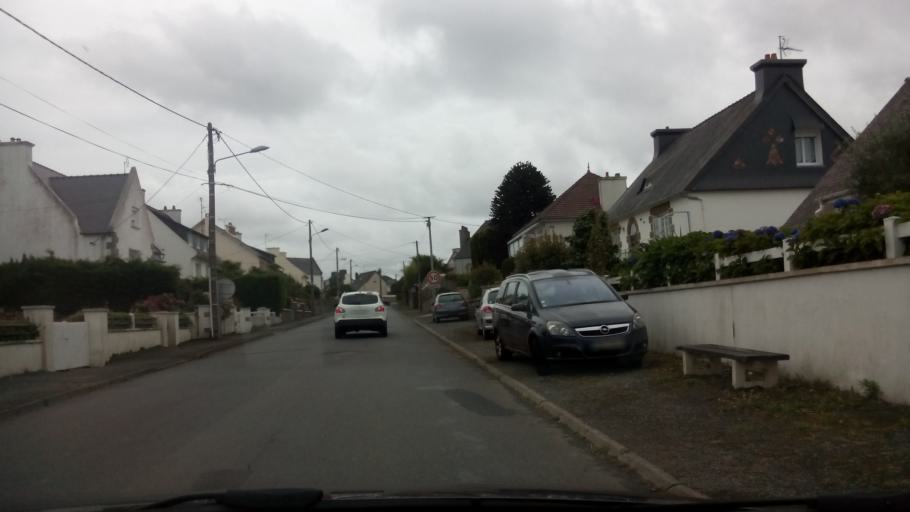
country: FR
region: Brittany
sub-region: Departement des Cotes-d'Armor
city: Plestin-les-Greves
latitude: 48.6656
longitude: -3.6318
